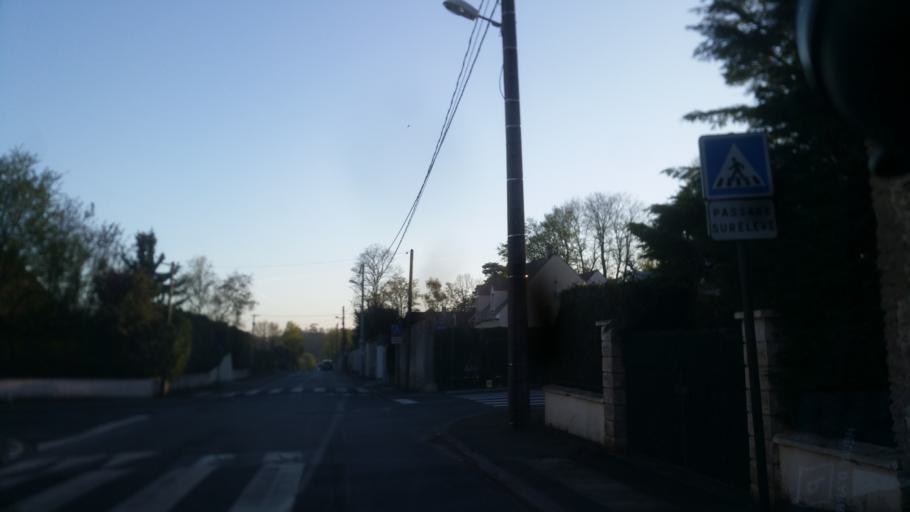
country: FR
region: Ile-de-France
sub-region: Departement de l'Essonne
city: Limours
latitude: 48.6402
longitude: 2.0730
